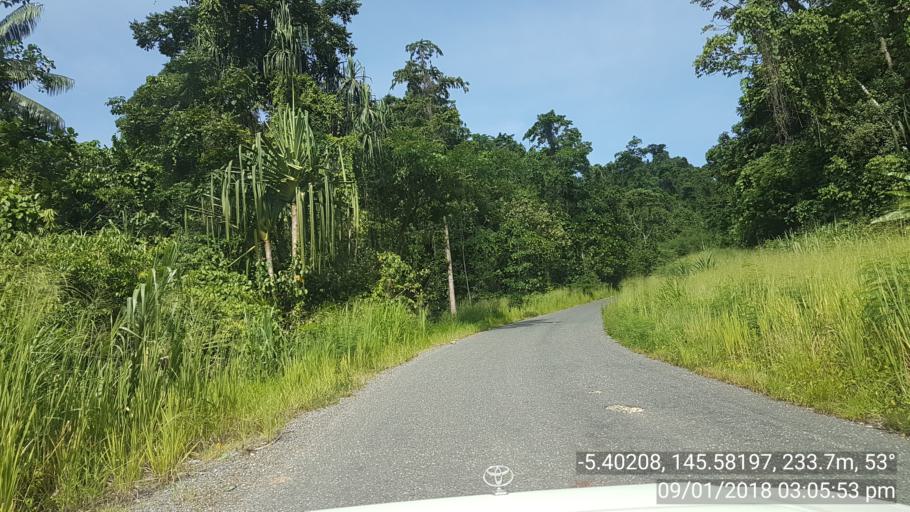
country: PG
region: Madang
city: Madang
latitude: -5.4019
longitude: 145.5819
